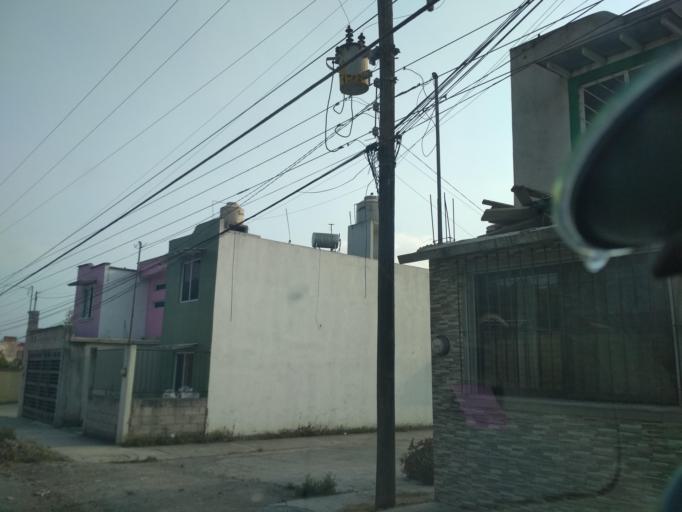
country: MX
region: Veracruz
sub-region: Ixhuatlancillo
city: Fraccionamiento Valle Dorado
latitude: 18.8659
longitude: -97.1174
